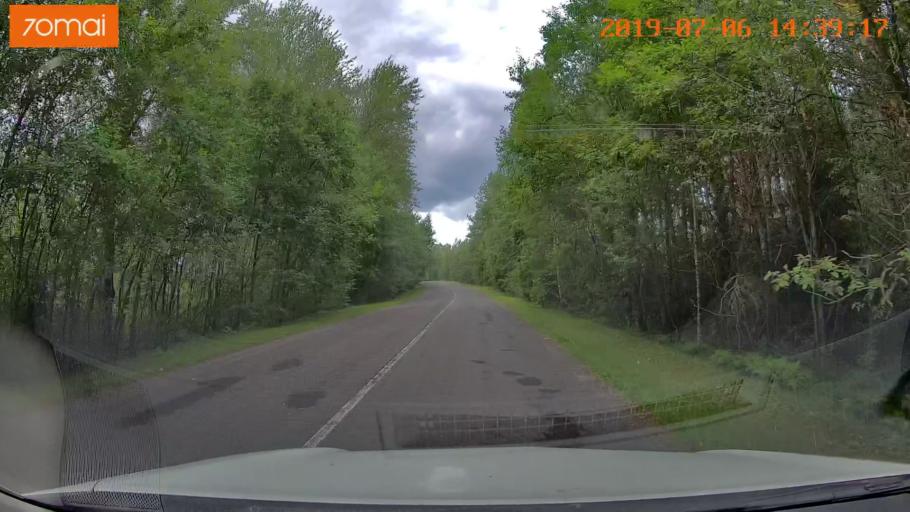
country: BY
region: Minsk
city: Ivyanyets
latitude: 53.9151
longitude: 26.6912
